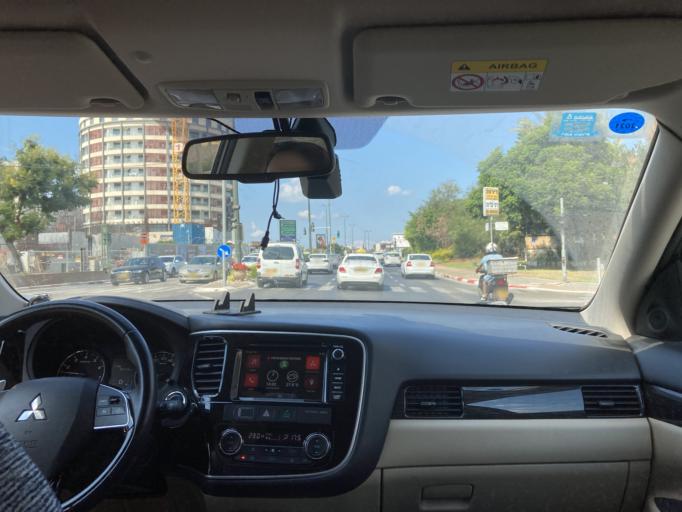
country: IL
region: Tel Aviv
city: Ramat HaSharon
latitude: 32.1220
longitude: 34.8250
